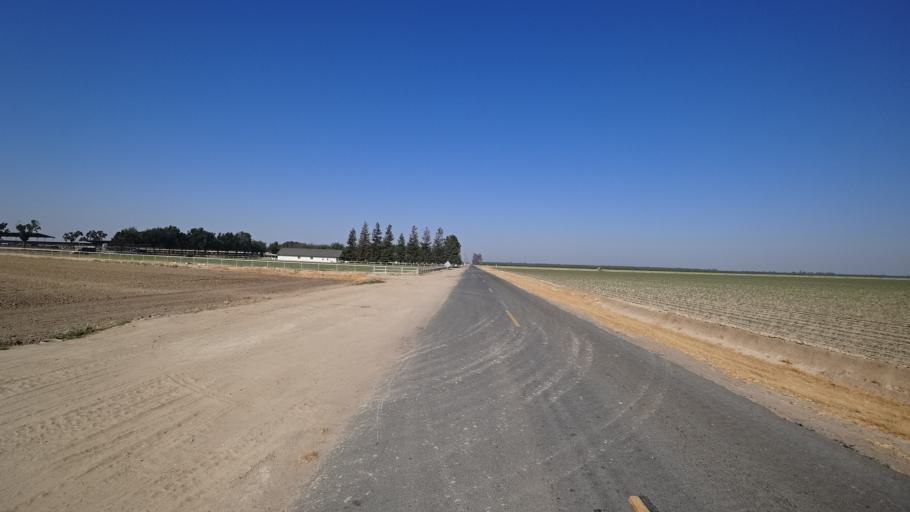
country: US
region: California
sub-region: Fresno County
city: Kingsburg
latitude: 36.4160
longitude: -119.5301
